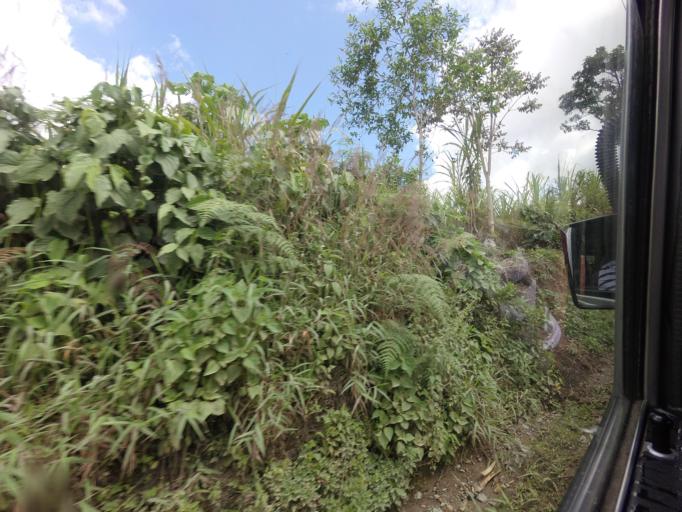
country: CO
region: Huila
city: Isnos
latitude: 1.9436
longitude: -76.2731
